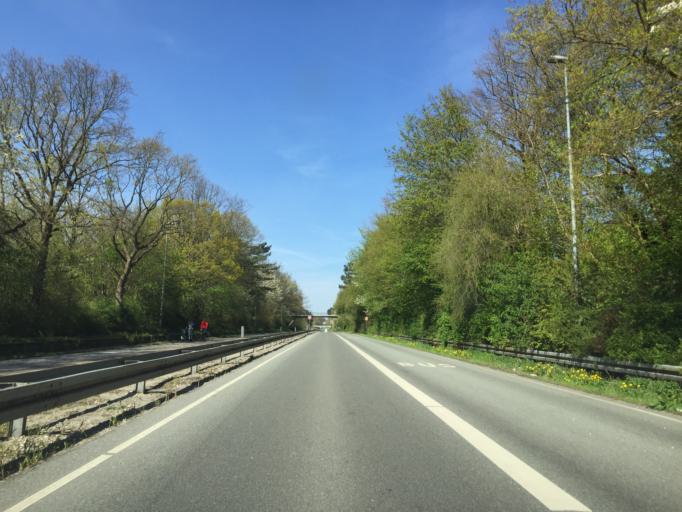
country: DK
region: Capital Region
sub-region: Gladsaxe Municipality
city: Buddinge
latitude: 55.7218
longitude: 12.4991
